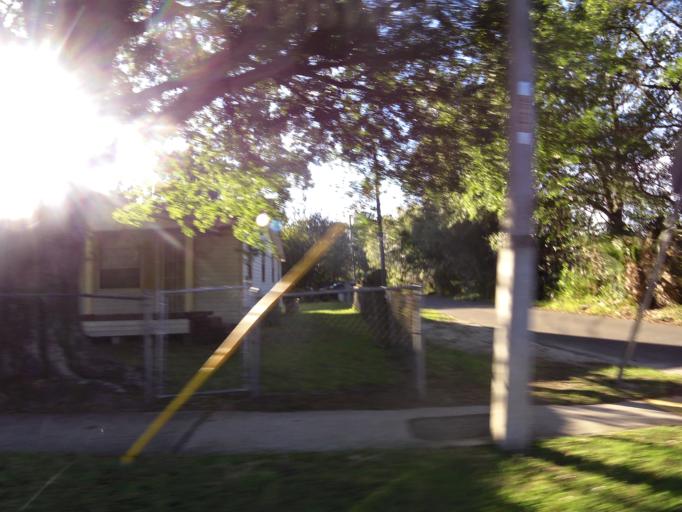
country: US
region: Florida
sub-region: Duval County
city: Jacksonville
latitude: 30.3519
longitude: -81.6863
